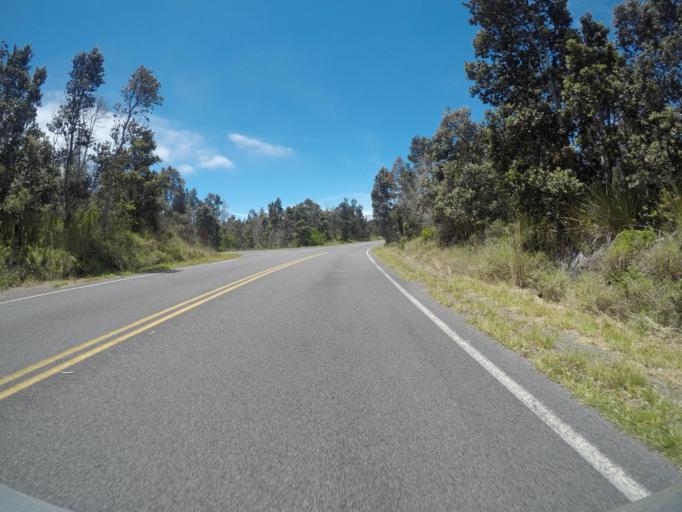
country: US
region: Hawaii
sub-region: Hawaii County
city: Volcano
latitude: 19.3663
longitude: -155.2222
